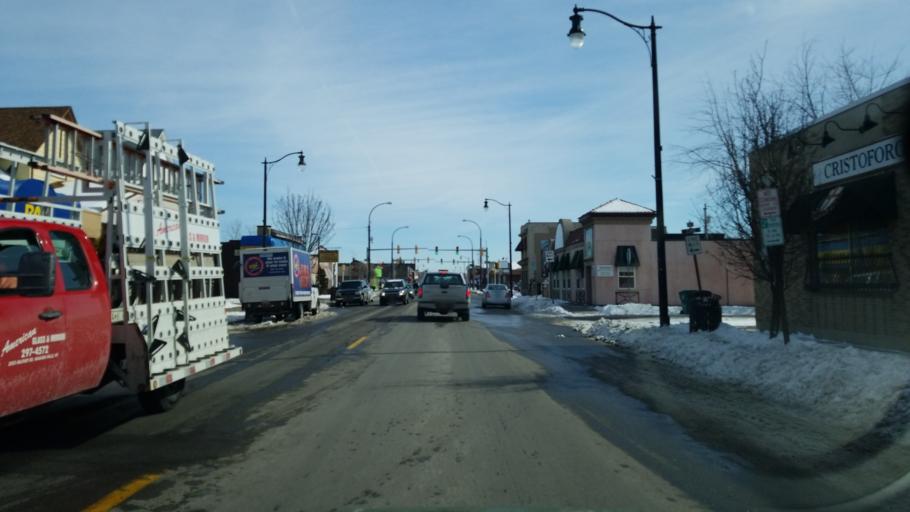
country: US
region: New York
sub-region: Niagara County
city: Niagara Falls
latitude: 43.0951
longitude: -79.0348
